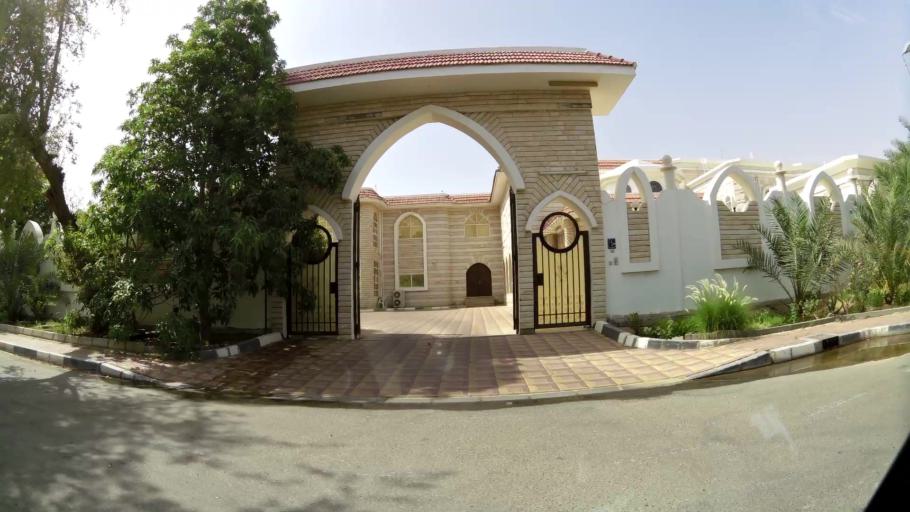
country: AE
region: Abu Dhabi
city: Al Ain
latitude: 24.1672
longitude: 55.6734
